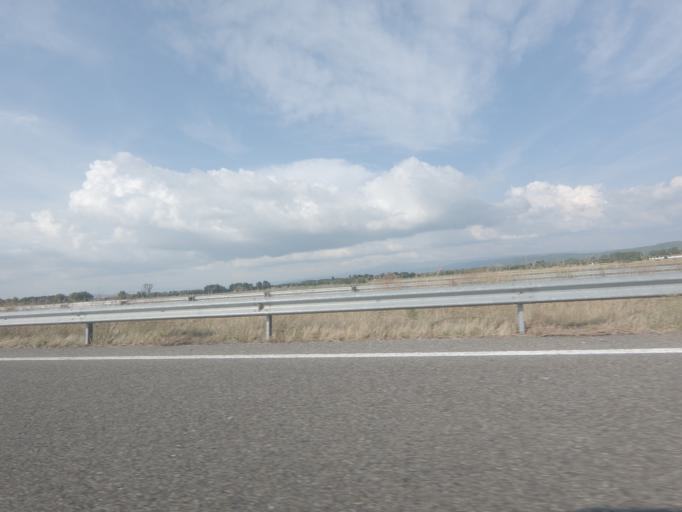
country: ES
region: Galicia
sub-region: Provincia de Ourense
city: Xinzo de Limia
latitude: 42.0903
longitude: -7.7225
